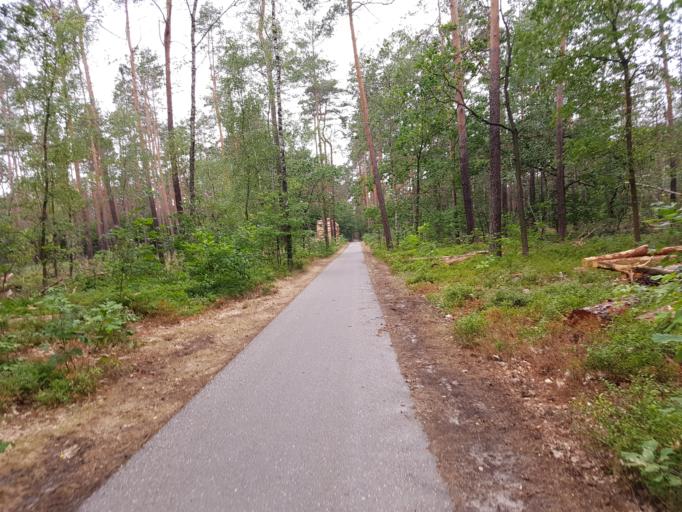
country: DE
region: Brandenburg
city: Finsterwalde
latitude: 51.6301
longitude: 13.6770
